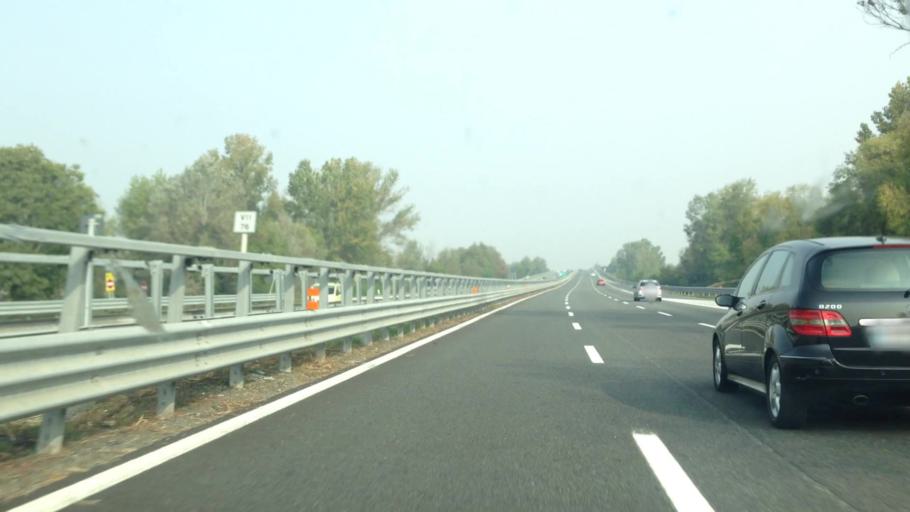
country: IT
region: Piedmont
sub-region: Provincia di Alessandria
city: Mirabello Monferrato
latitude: 45.0180
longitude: 8.5358
